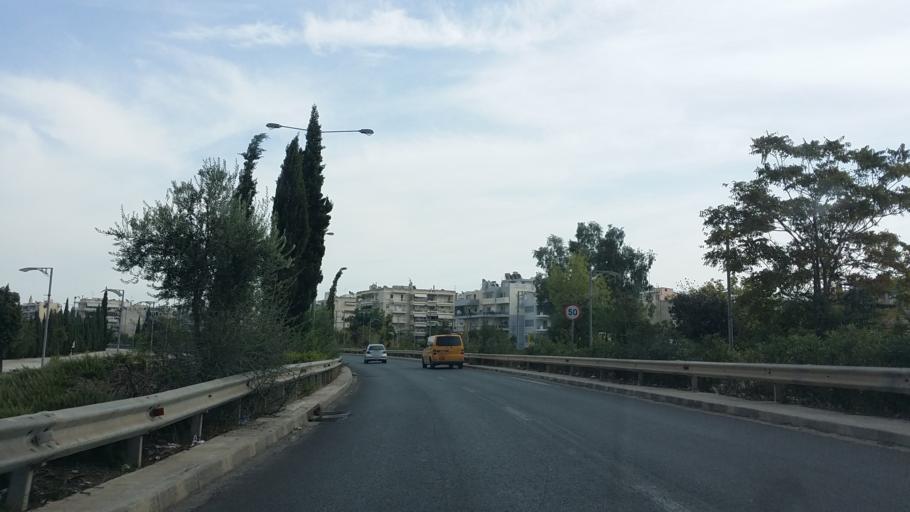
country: GR
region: Attica
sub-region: Nomarchia Athinas
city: Filothei
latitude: 38.0361
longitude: 23.7809
